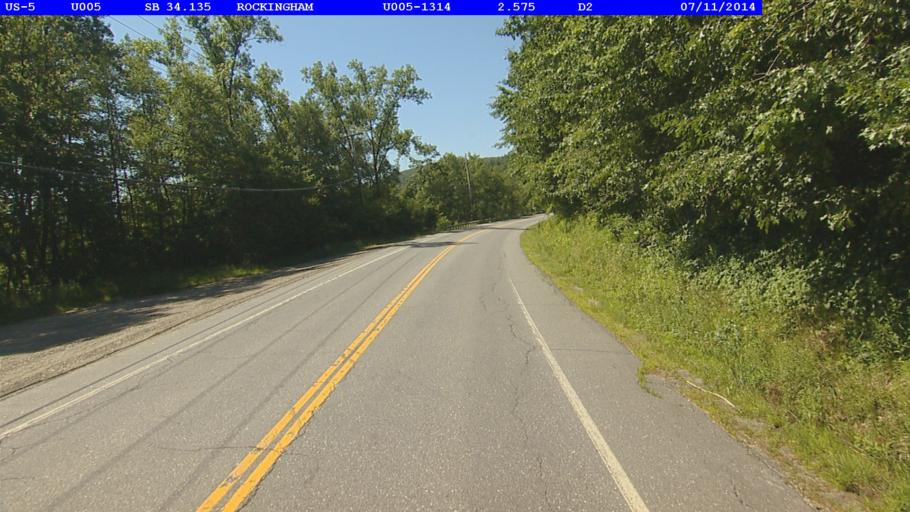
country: US
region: Vermont
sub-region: Windham County
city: Bellows Falls
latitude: 43.1581
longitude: -72.4576
